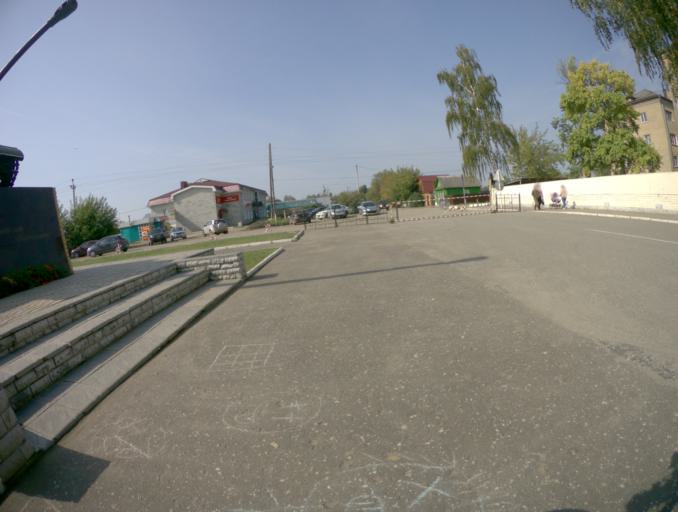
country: RU
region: Vladimir
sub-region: Kovrovskiy Rayon
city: Kovrov
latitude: 56.3834
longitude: 41.3245
